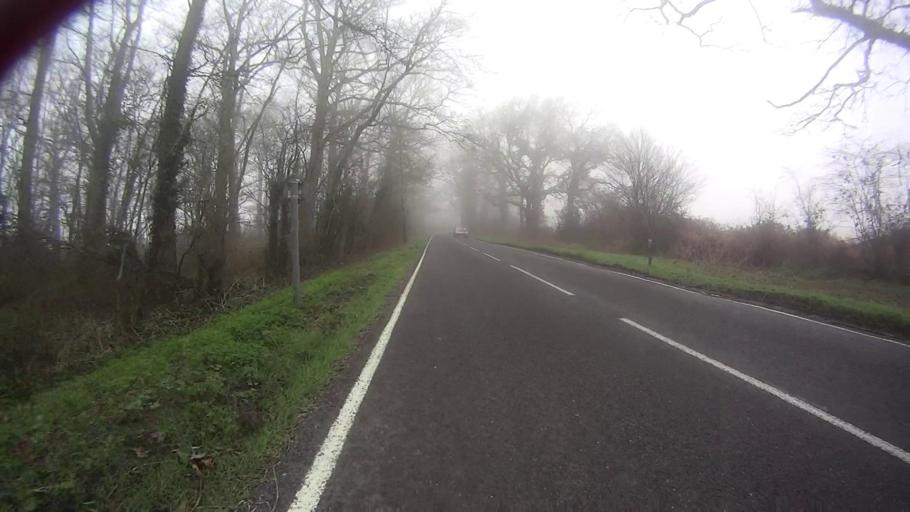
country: GB
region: England
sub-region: Surrey
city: Newdigate
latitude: 51.1352
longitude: -0.3160
